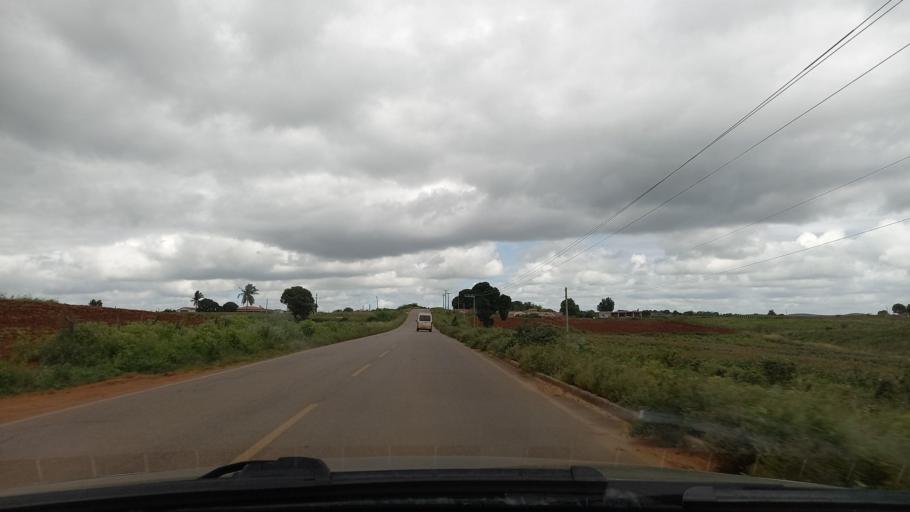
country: BR
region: Sergipe
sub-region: Caninde De Sao Francisco
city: Caninde de Sao Francisco
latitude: -9.6744
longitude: -37.8013
